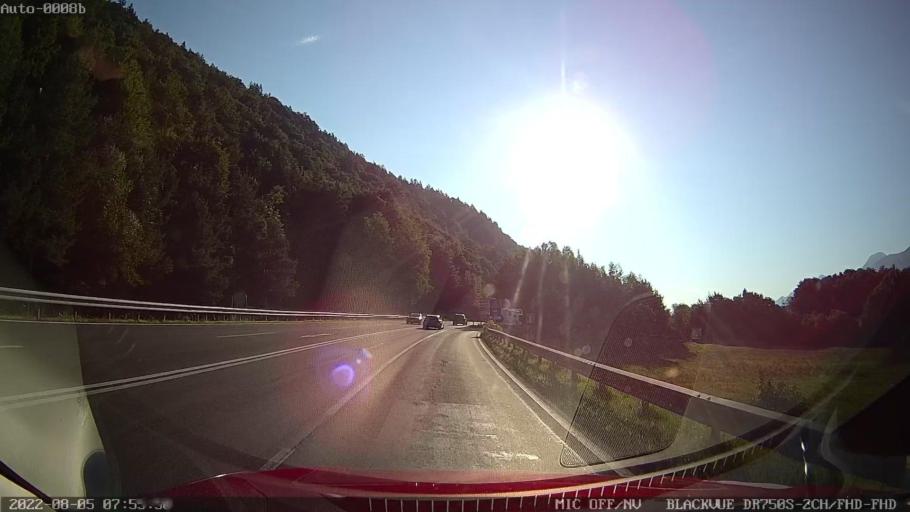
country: AT
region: Carinthia
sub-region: Politischer Bezirk Villach Land
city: Finkenstein am Faaker See
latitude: 46.5746
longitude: 13.8222
